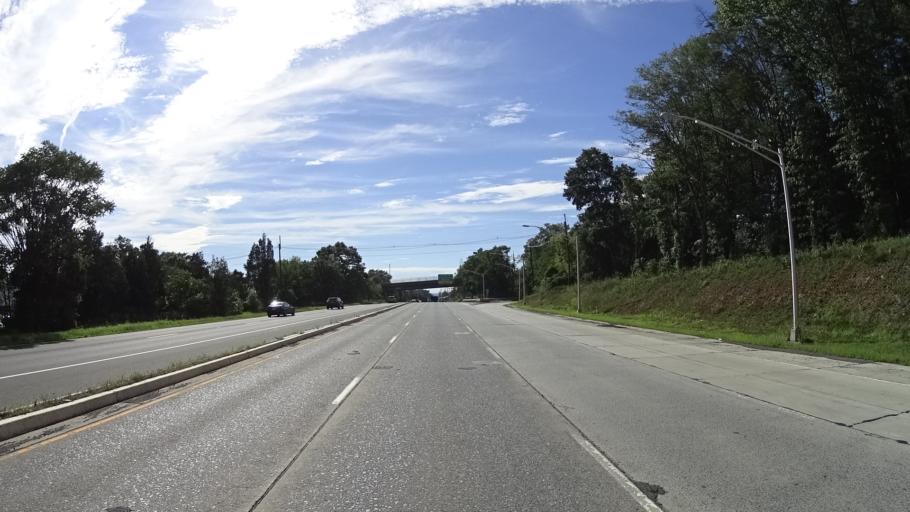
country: US
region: New Jersey
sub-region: Somerset County
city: Finderne
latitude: 40.5770
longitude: -74.5737
